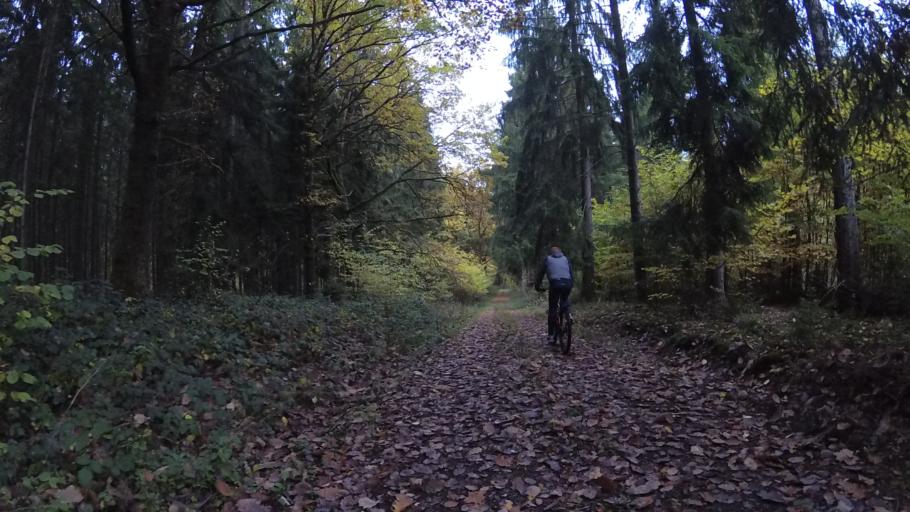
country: DE
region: Saarland
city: Sankt Wendel
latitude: 49.4533
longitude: 7.2087
